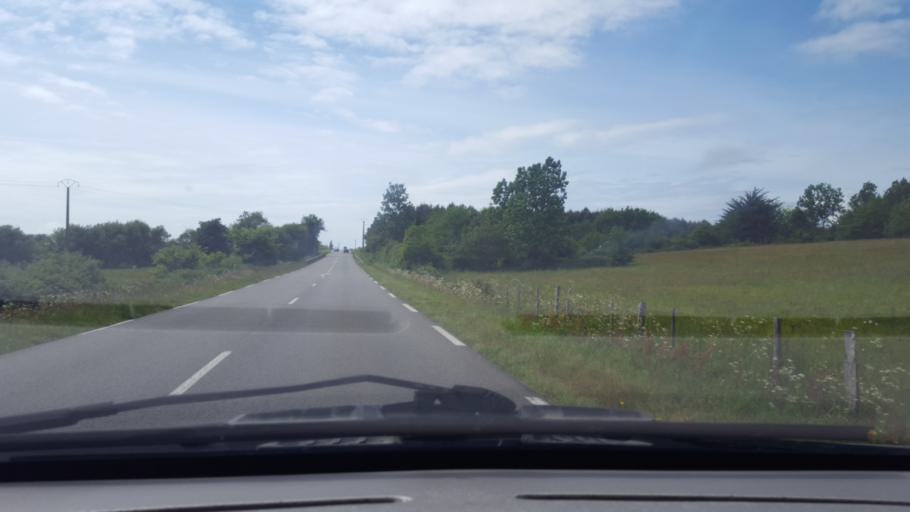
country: FR
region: Pays de la Loire
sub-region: Departement de la Loire-Atlantique
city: Bourgneuf-en-Retz
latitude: 47.0310
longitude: -1.9129
